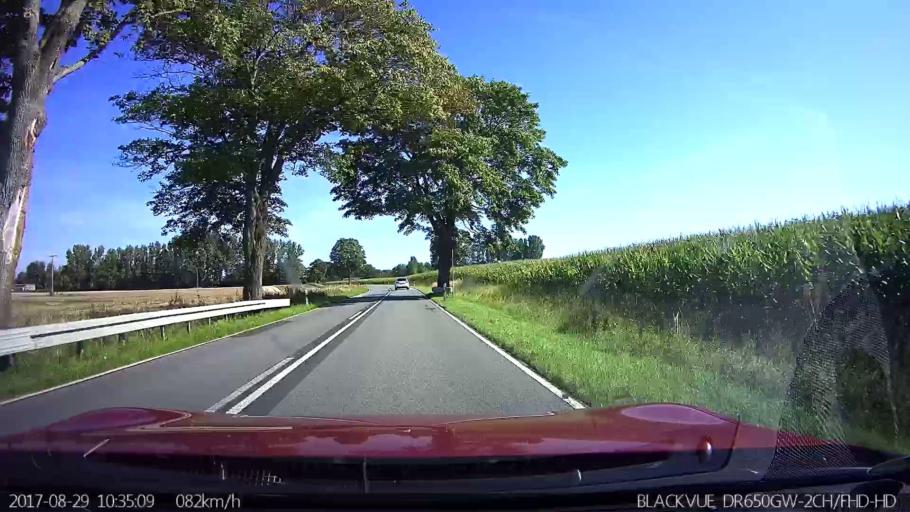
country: DE
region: Mecklenburg-Vorpommern
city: Tribsees
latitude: 54.1344
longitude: 12.7951
